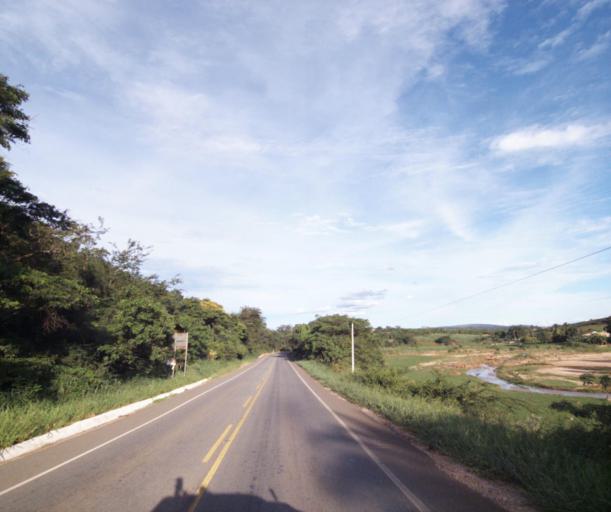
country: BR
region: Bahia
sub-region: Caetite
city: Caetite
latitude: -14.0666
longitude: -42.4695
